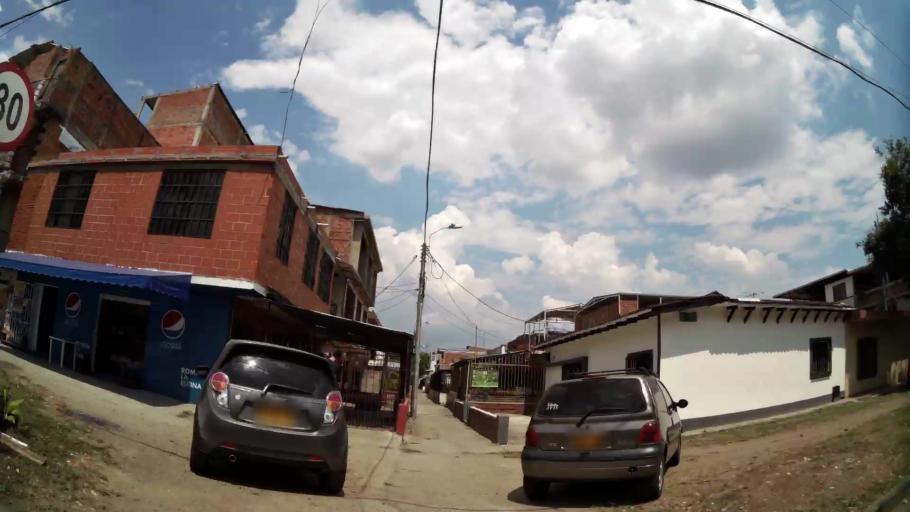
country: CO
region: Valle del Cauca
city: Cali
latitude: 3.4639
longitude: -76.5048
